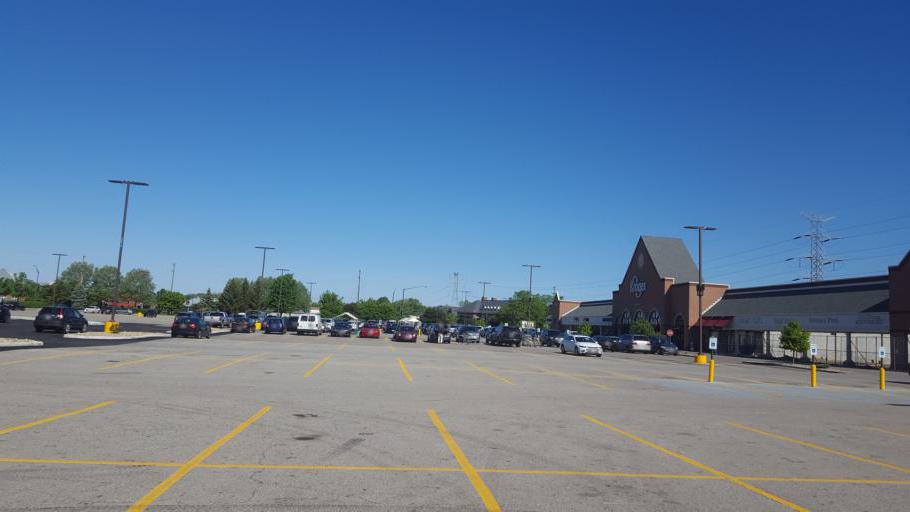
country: US
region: Ohio
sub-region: Franklin County
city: Westerville
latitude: 40.1485
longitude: -82.9202
